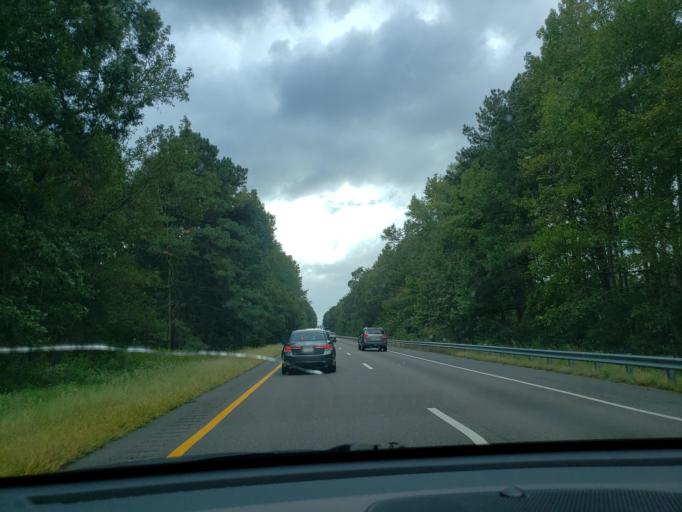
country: US
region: Virginia
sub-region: Mecklenburg County
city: Bracey
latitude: 36.6568
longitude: -78.1344
